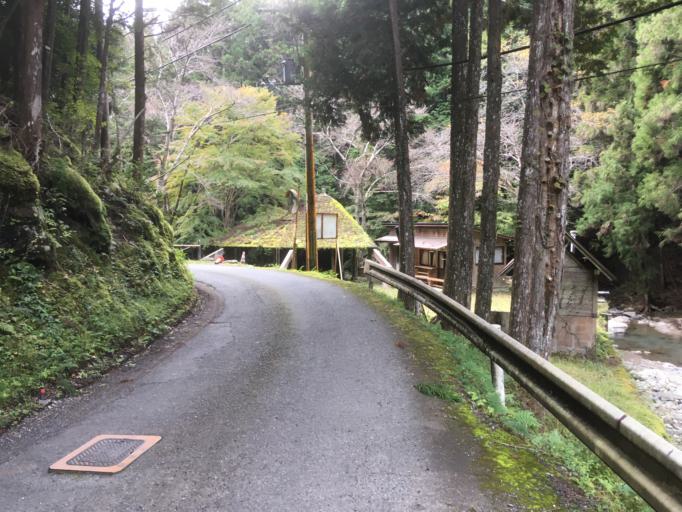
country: JP
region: Nara
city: Yoshino-cho
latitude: 34.3909
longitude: 135.9904
